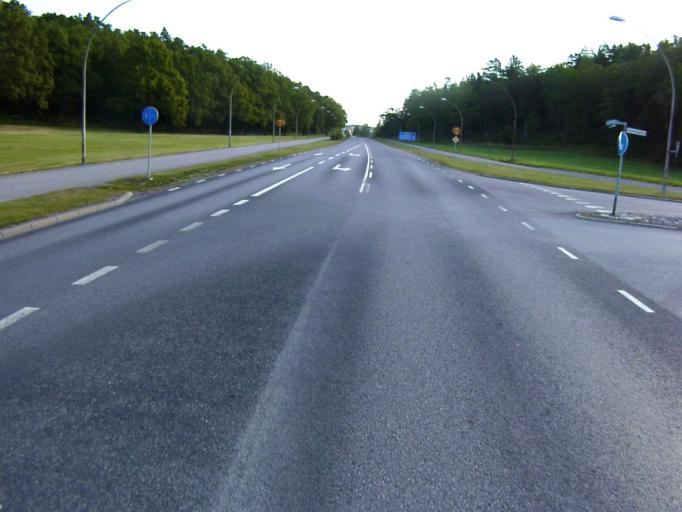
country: SE
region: Soedermanland
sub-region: Eskilstuna Kommun
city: Eskilstuna
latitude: 59.3662
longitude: 16.5369
